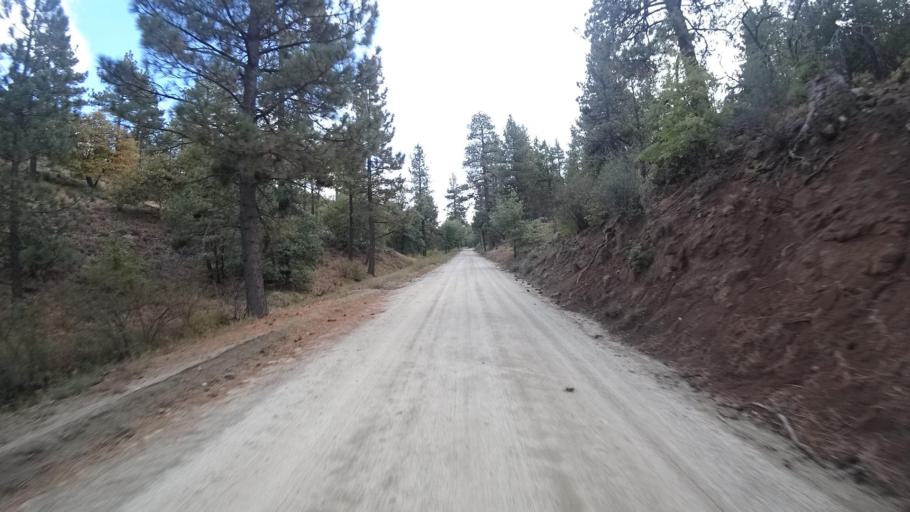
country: US
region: California
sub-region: San Diego County
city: Pine Valley
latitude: 32.8726
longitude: -116.4257
